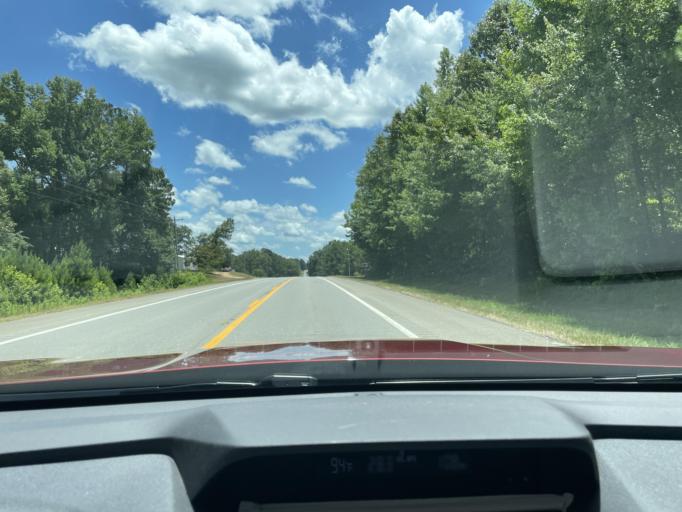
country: US
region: Arkansas
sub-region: Drew County
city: Monticello
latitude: 33.7393
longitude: -91.8197
